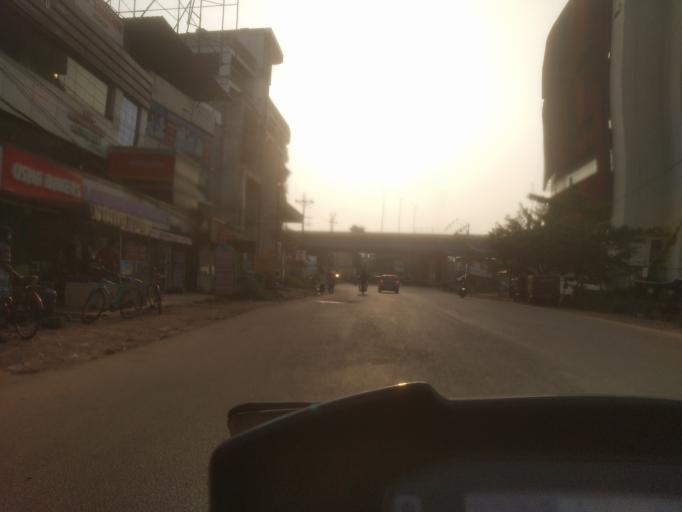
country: IN
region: Kerala
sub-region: Ernakulam
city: Cochin
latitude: 9.9370
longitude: 76.3192
